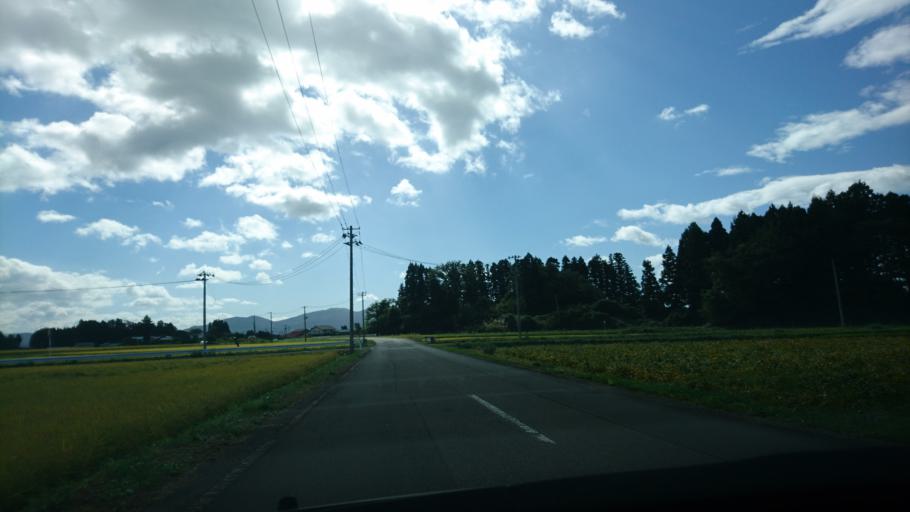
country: JP
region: Iwate
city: Mizusawa
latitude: 39.0799
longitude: 141.1038
